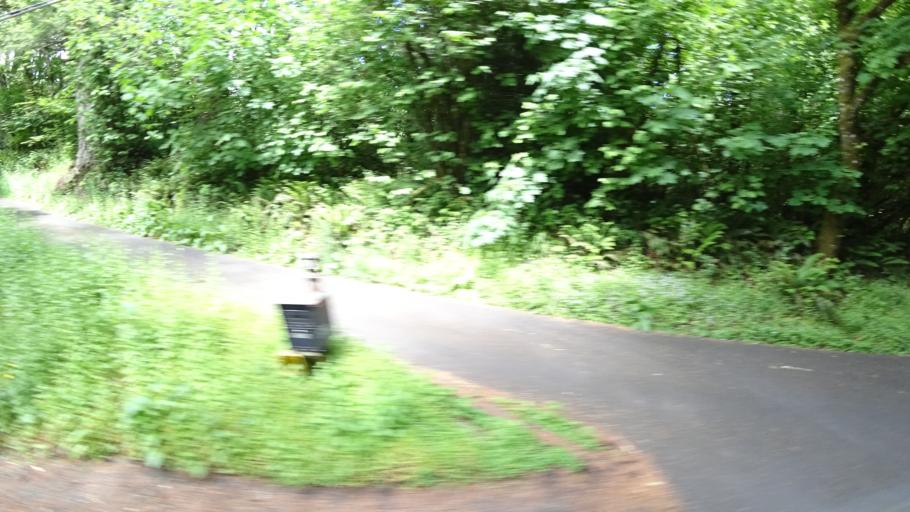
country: US
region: Oregon
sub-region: Washington County
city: Oak Hills
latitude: 45.5850
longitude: -122.8032
